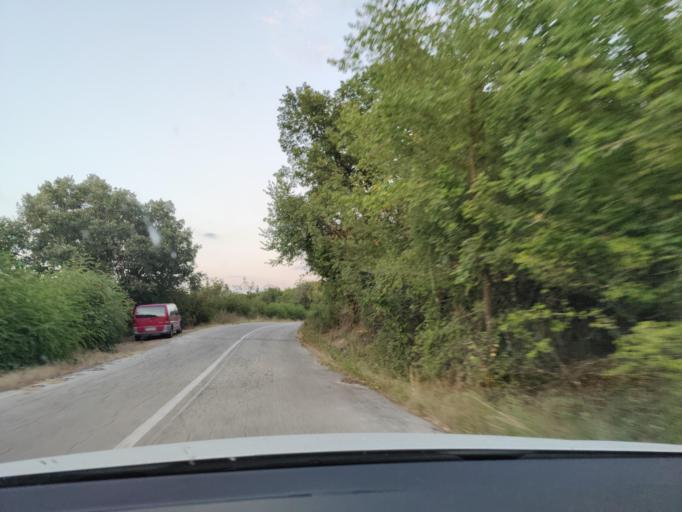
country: GR
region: Central Macedonia
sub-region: Nomos Serron
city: Chrysochorafa
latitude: 41.1807
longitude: 23.1557
